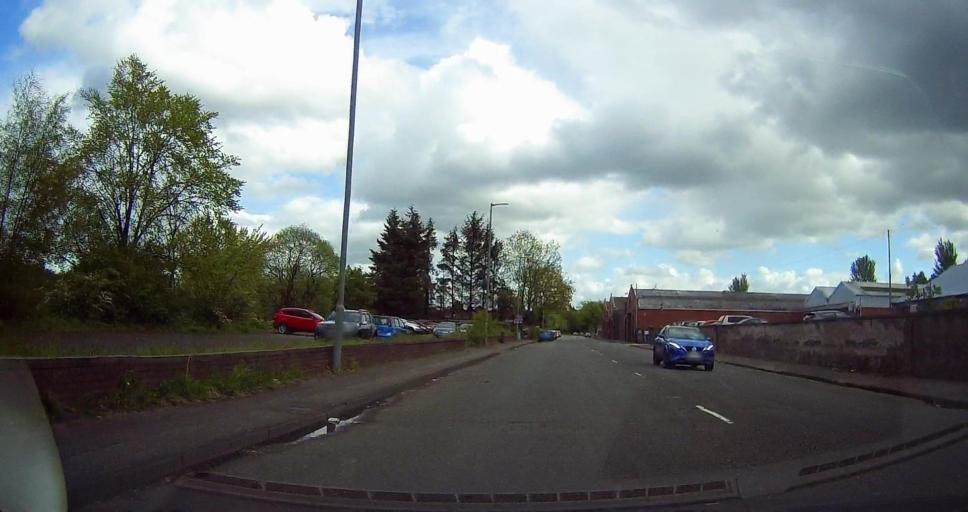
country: GB
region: Scotland
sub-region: Falkirk
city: Larbert
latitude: 56.0139
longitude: -3.8268
